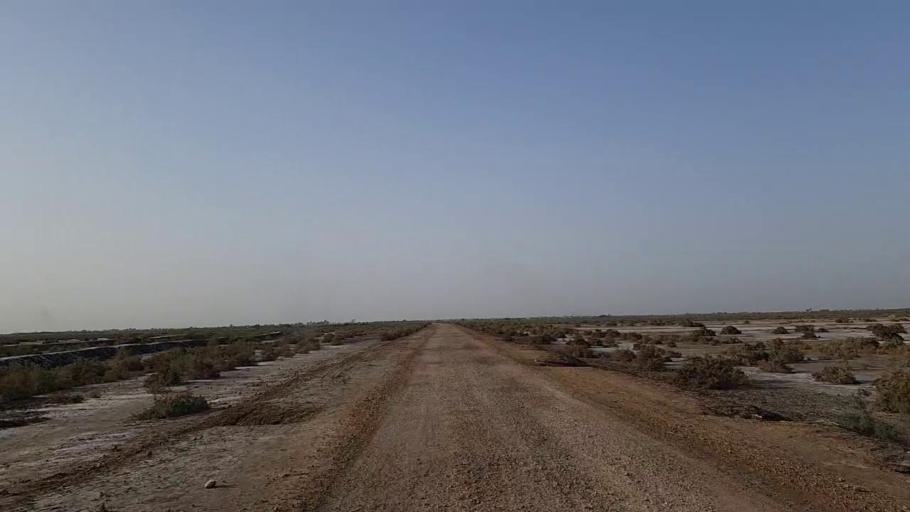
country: PK
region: Sindh
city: Jati
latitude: 24.3565
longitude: 68.1478
